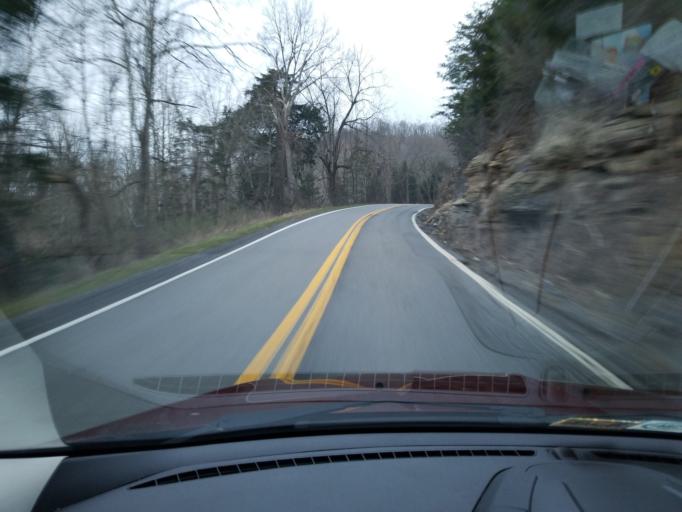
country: US
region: West Virginia
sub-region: Monroe County
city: Union
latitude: 37.5471
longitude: -80.5873
